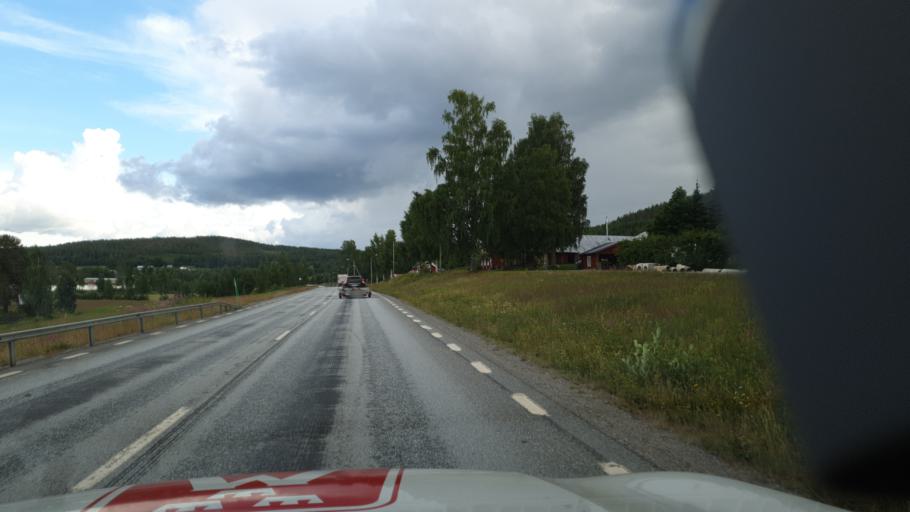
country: SE
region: Vaesterbotten
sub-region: Vannas Kommun
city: Vannasby
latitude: 64.0009
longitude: 20.0349
